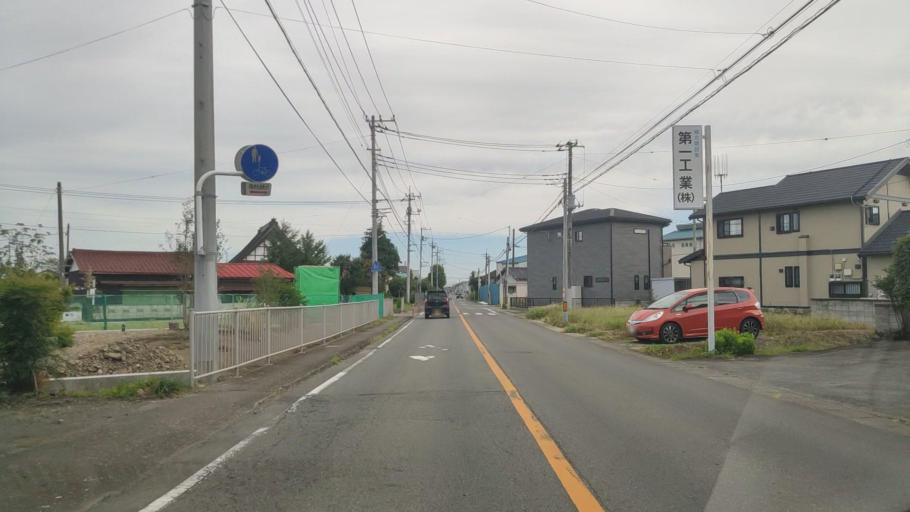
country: JP
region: Gunma
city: Takasaki
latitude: 36.3627
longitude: 138.9784
